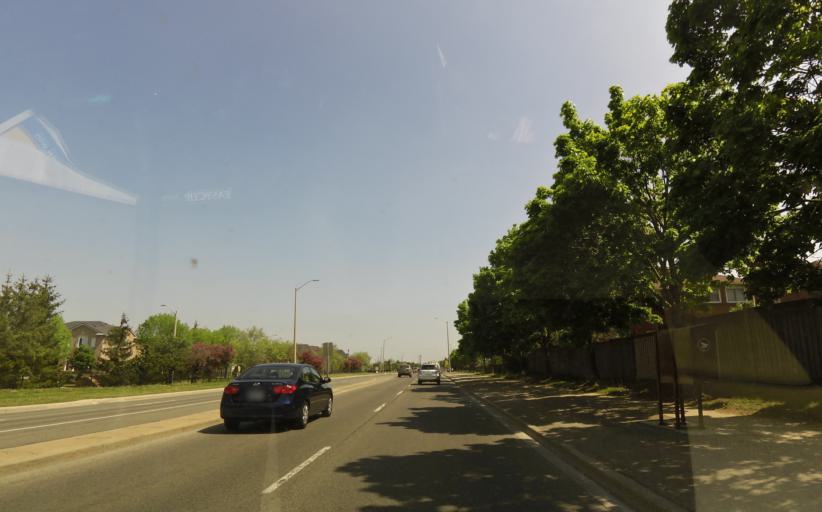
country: CA
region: Ontario
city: Mississauga
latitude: 43.6183
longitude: -79.6450
